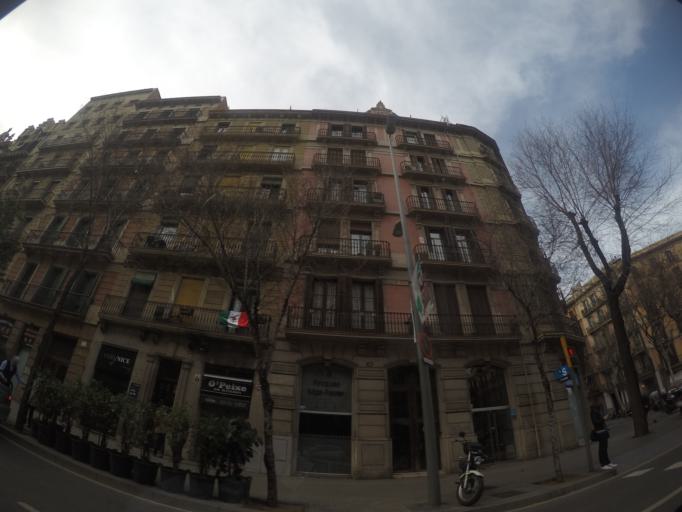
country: ES
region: Catalonia
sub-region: Provincia de Barcelona
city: Barcelona
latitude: 41.3882
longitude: 2.1595
